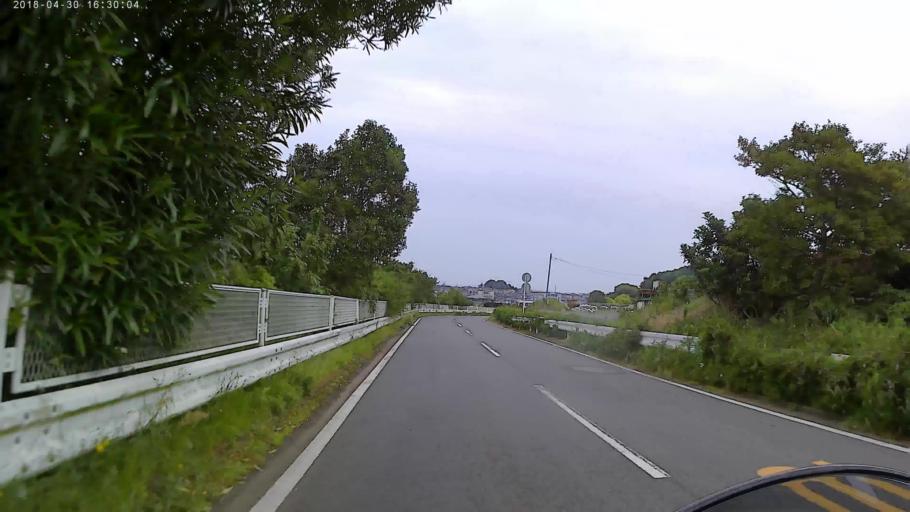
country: JP
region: Kanagawa
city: Zama
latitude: 35.4567
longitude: 139.4053
